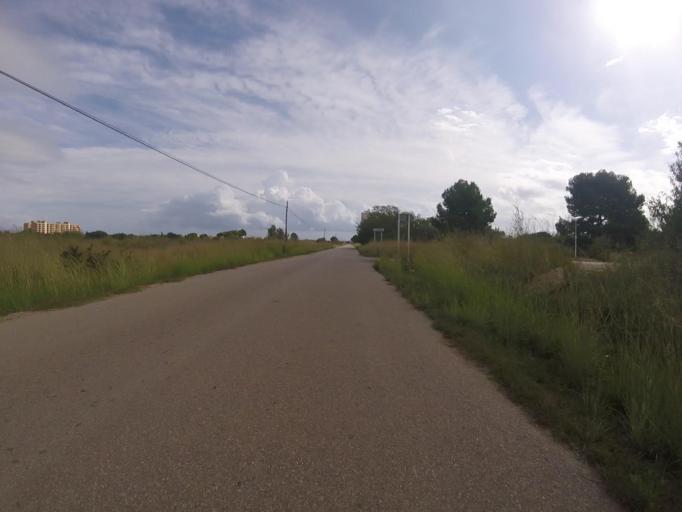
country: ES
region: Valencia
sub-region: Provincia de Castello
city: Orpesa/Oropesa del Mar
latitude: 40.1326
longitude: 0.1581
